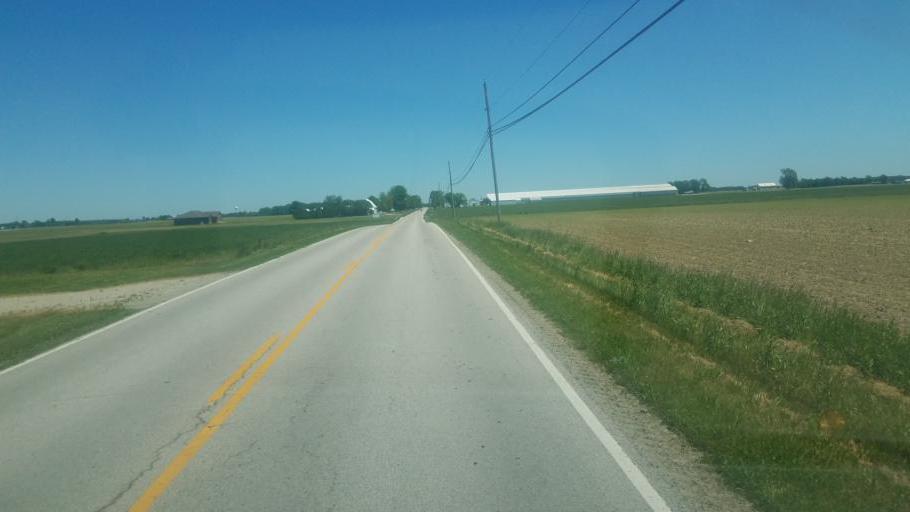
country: US
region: Ohio
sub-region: Darke County
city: Versailles
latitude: 40.2262
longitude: -84.4460
